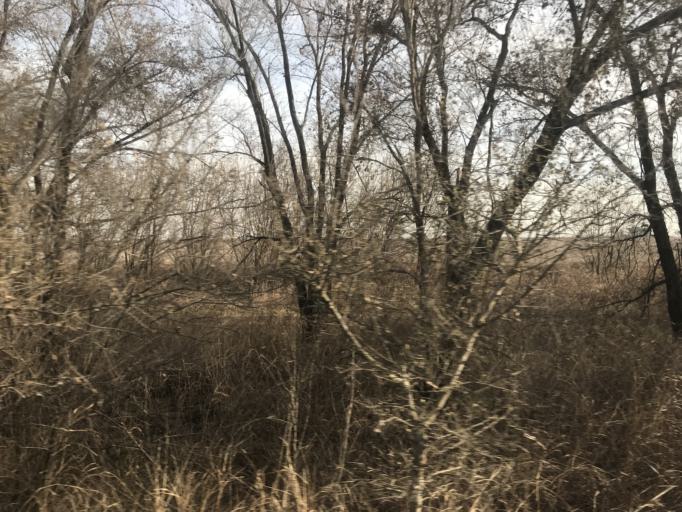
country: AR
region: Cordoba
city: Laguna Larga
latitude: -31.7370
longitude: -63.8379
